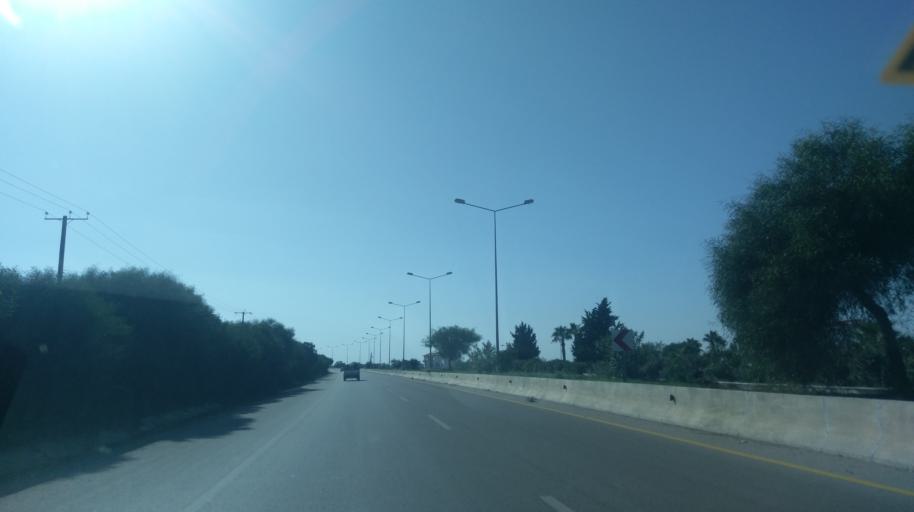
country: CY
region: Ammochostos
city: Trikomo
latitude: 35.2386
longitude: 33.8991
